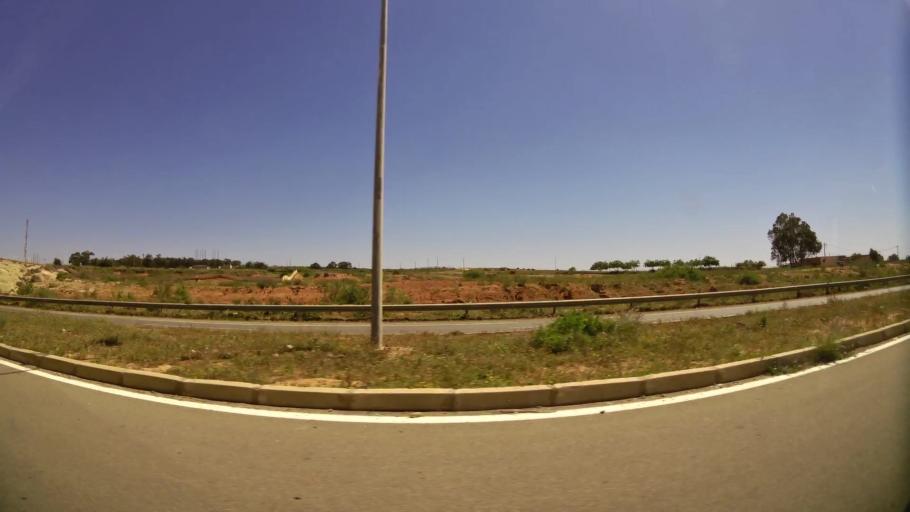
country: MA
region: Oriental
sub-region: Berkane-Taourirt
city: Madagh
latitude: 35.1000
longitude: -2.3312
